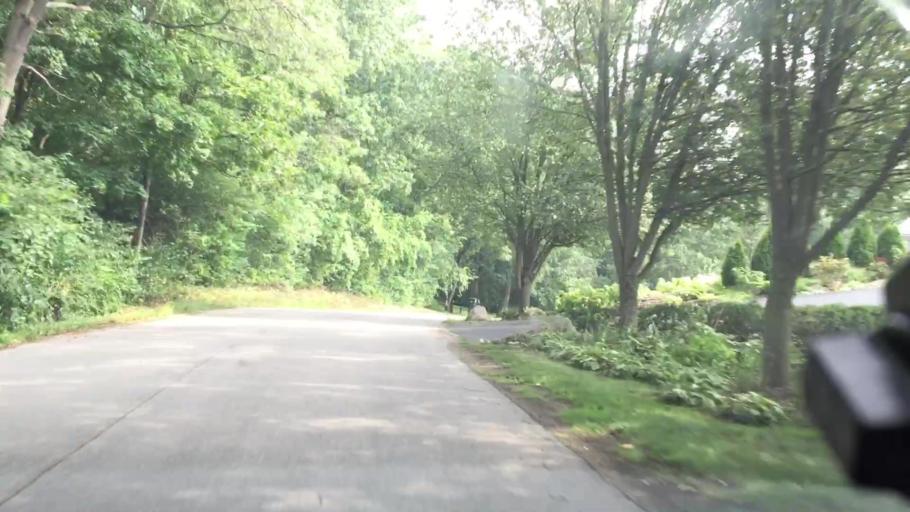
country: US
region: Michigan
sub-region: Oakland County
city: Sylvan Lake
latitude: 42.5987
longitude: -83.2917
